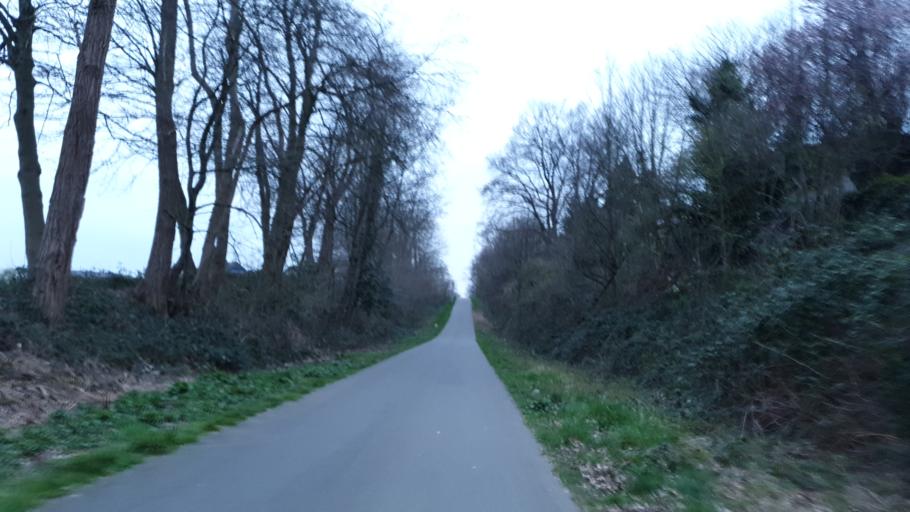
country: DE
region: North Rhine-Westphalia
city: Burscheid
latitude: 51.0835
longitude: 7.1063
